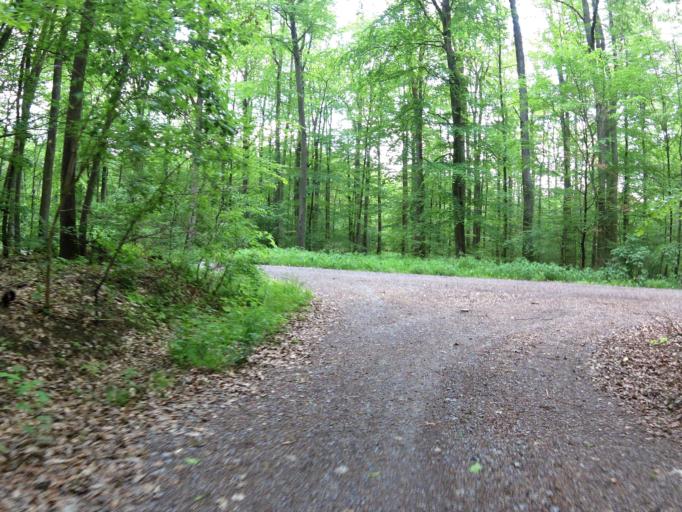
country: DE
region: Bavaria
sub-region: Regierungsbezirk Unterfranken
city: Kist
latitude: 49.7449
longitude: 9.8616
